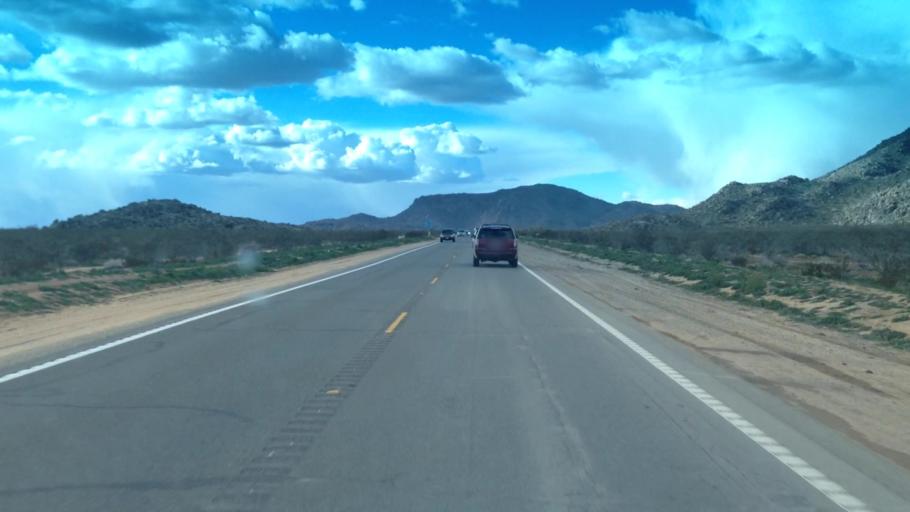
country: US
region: California
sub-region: San Bernardino County
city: Lucerne Valley
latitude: 34.4596
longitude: -117.0775
